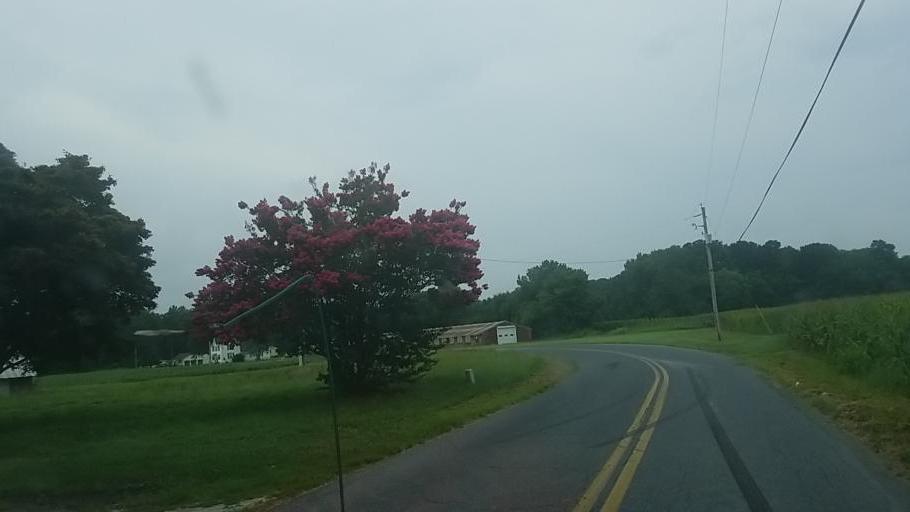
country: US
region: Delaware
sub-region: Sussex County
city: Selbyville
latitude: 38.4379
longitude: -75.1943
